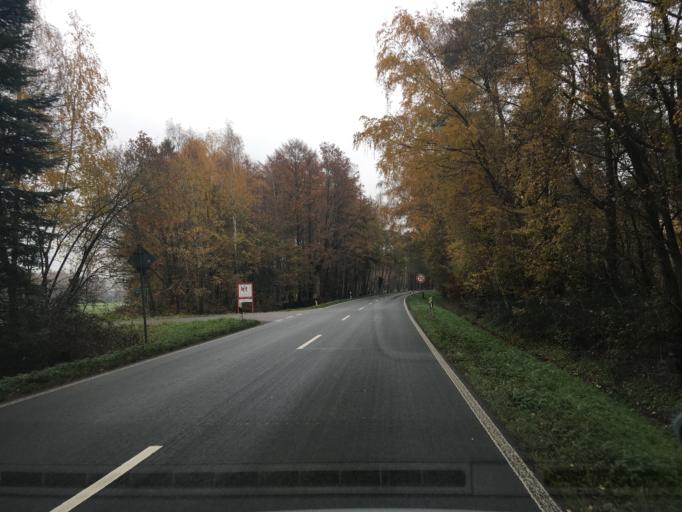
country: DE
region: North Rhine-Westphalia
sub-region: Regierungsbezirk Munster
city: Legden
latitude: 52.0268
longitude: 7.0661
